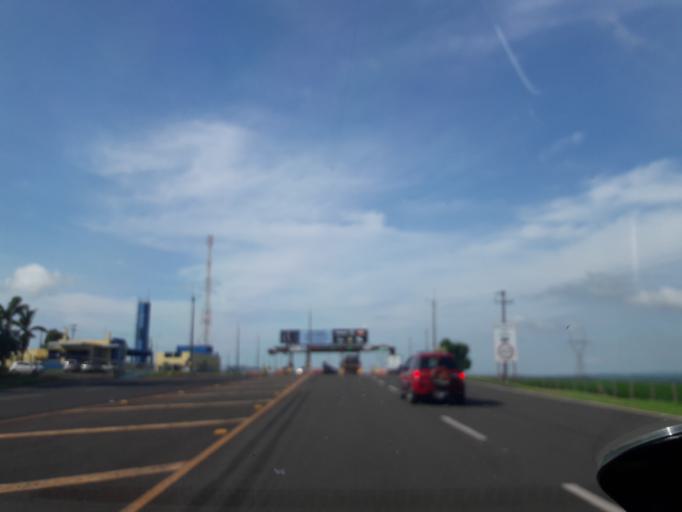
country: BR
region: Parana
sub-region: Paicandu
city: Paicandu
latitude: -23.6352
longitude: -52.1066
